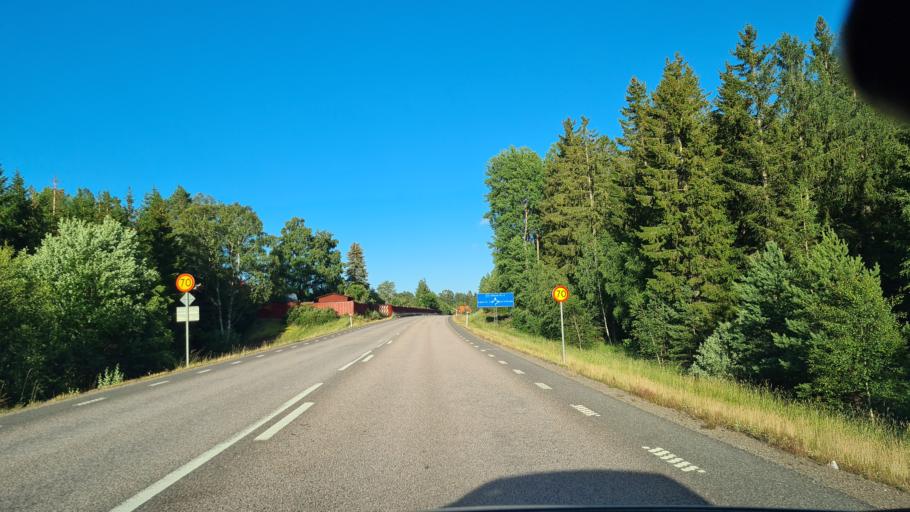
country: SE
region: Soedermanland
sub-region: Gnesta Kommun
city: Gnesta
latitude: 59.0491
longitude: 17.2752
